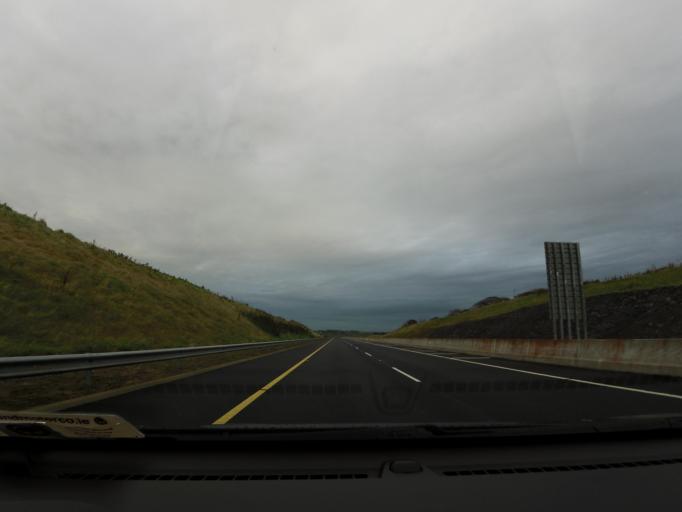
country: IE
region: Connaught
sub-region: County Galway
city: Tuam
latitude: 53.4104
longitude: -8.8267
